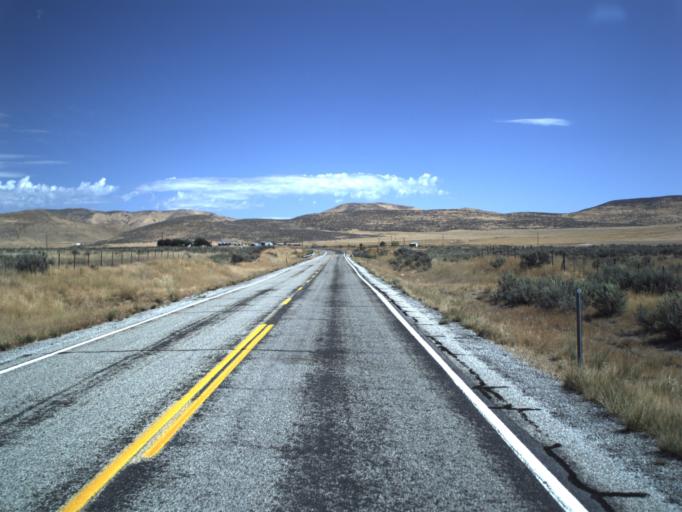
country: US
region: Utah
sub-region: Box Elder County
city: Garland
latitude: 41.7918
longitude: -112.4215
